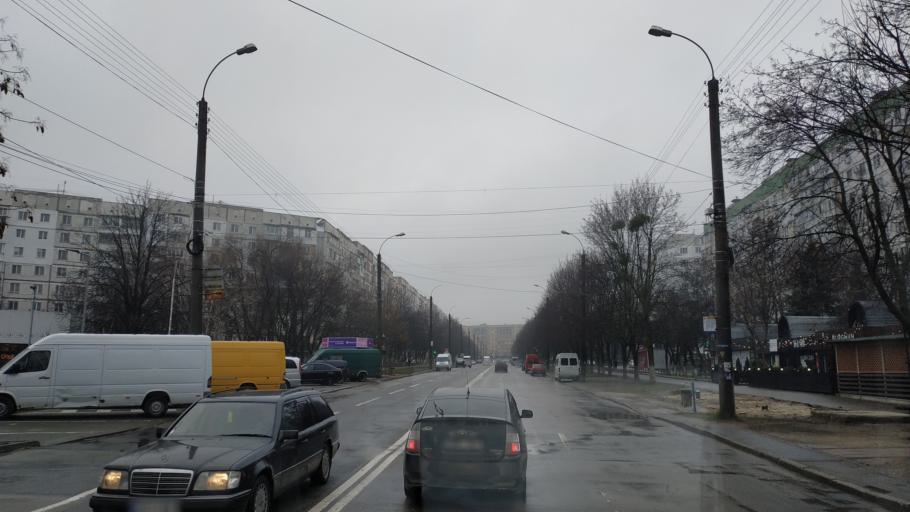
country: MD
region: Chisinau
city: Vatra
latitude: 47.0429
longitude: 28.7702
